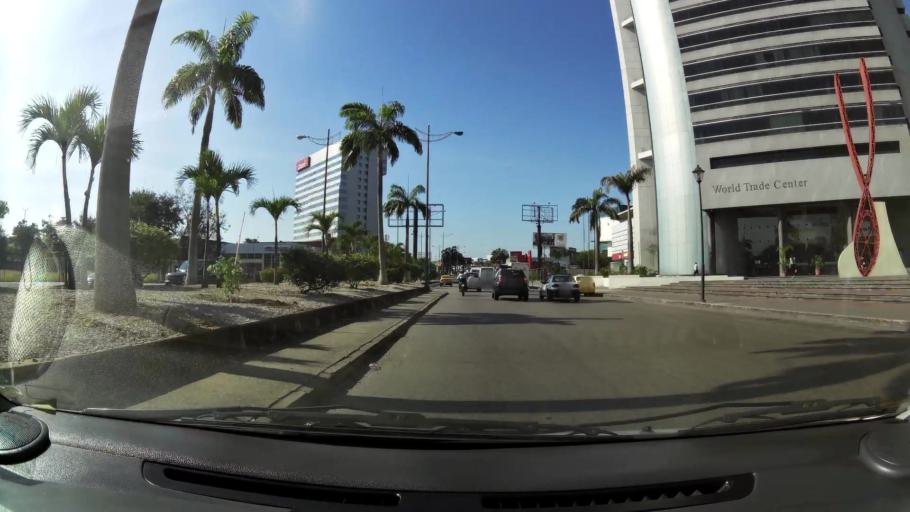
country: EC
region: Guayas
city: Guayaquil
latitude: -2.1632
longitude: -79.8975
